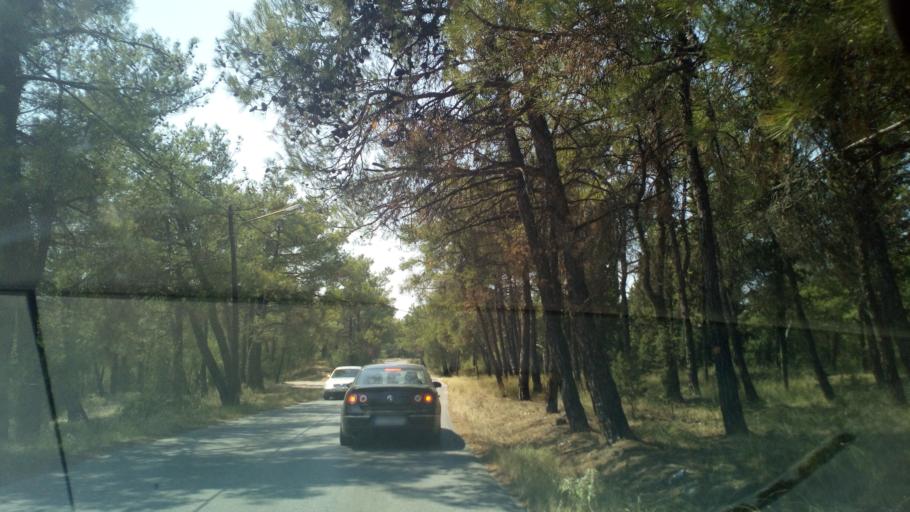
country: GR
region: Central Macedonia
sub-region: Nomos Thessalonikis
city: Agios Pavlos
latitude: 40.6433
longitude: 22.9762
